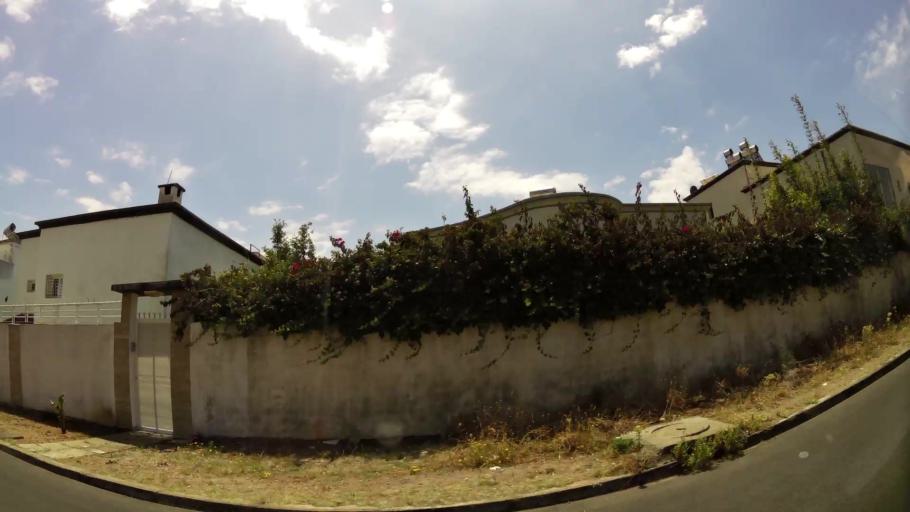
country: MA
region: Gharb-Chrarda-Beni Hssen
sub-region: Kenitra Province
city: Kenitra
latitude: 34.2671
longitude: -6.6119
